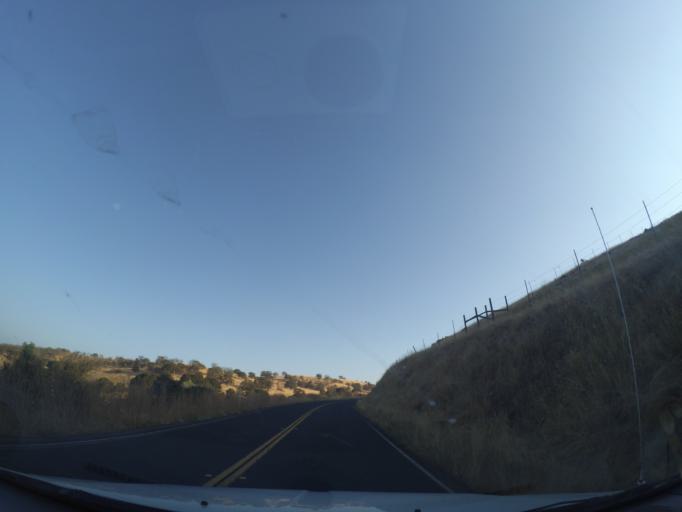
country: US
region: California
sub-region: Merced County
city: Planada
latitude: 37.4982
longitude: -120.2393
